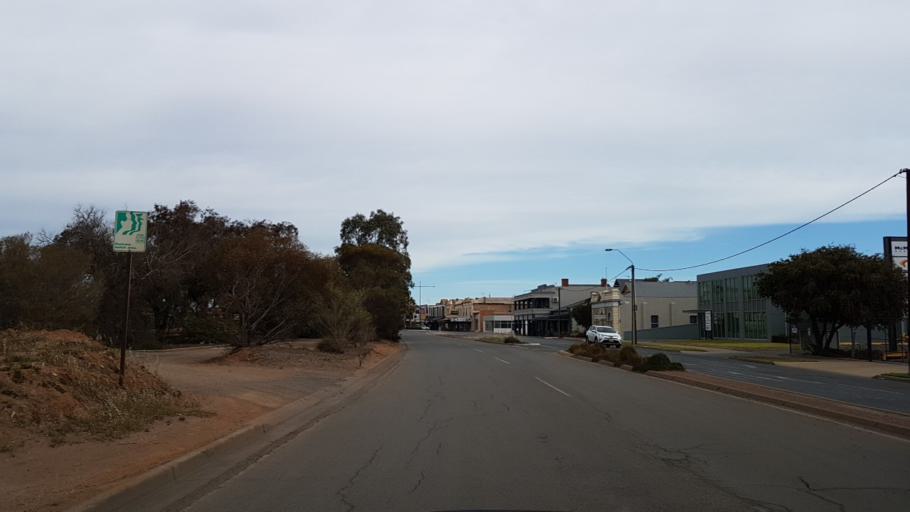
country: AU
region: South Australia
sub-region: Port Pirie City and Dists
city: Port Pirie
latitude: -33.1739
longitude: 138.0102
